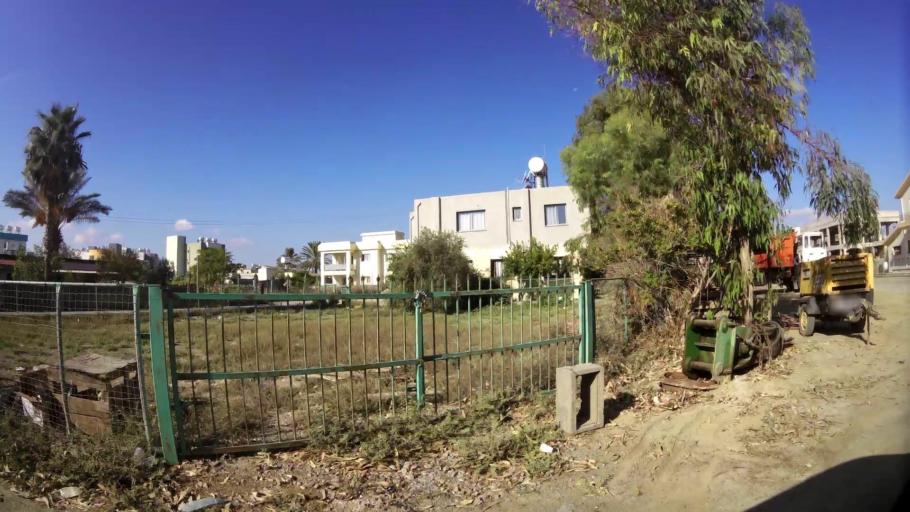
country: CY
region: Lefkosia
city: Nicosia
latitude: 35.2137
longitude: 33.3056
